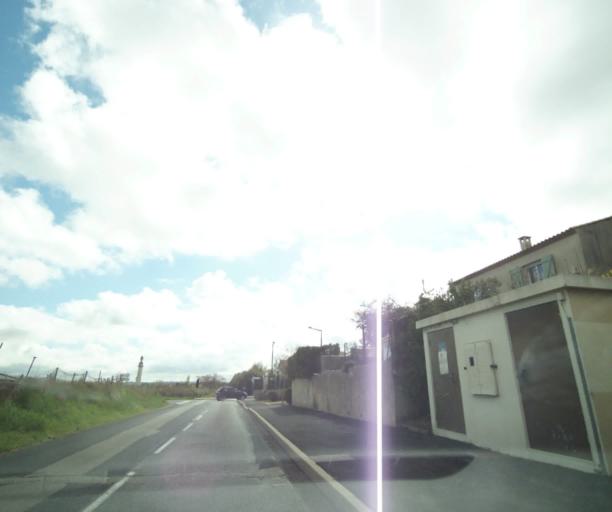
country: FR
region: Languedoc-Roussillon
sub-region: Departement de l'Herault
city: Pignan
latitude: 43.5795
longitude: 3.7553
